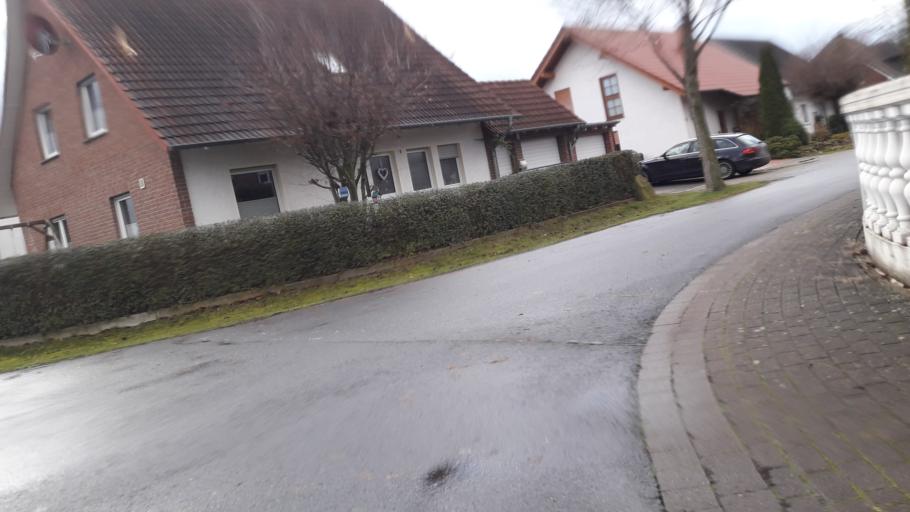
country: DE
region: North Rhine-Westphalia
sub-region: Regierungsbezirk Detmold
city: Petershagen
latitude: 52.3444
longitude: 8.9670
